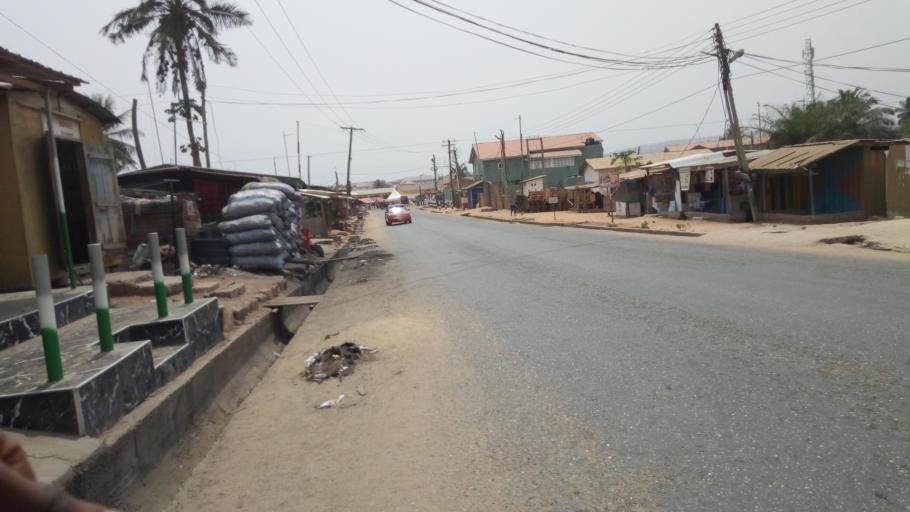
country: GH
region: Greater Accra
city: Gbawe
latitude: 5.5596
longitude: -0.3099
